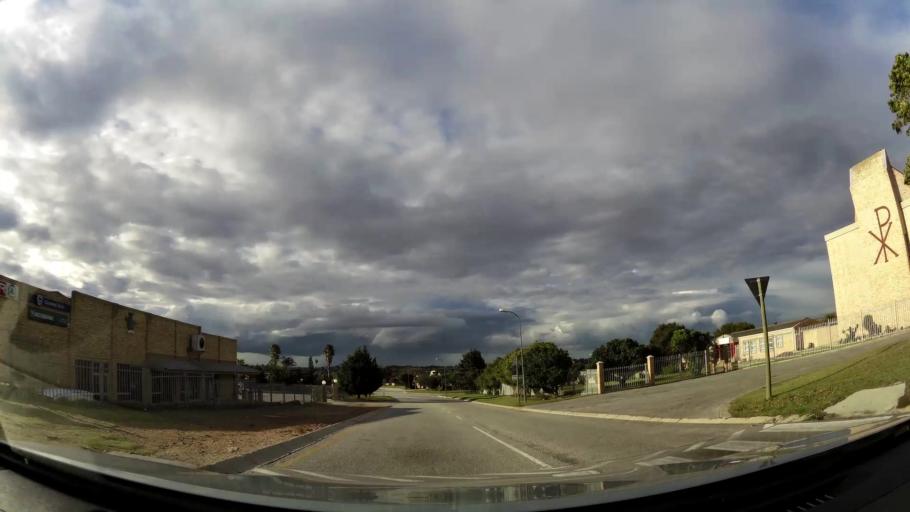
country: ZA
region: Eastern Cape
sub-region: Nelson Mandela Bay Metropolitan Municipality
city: Port Elizabeth
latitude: -33.9590
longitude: 25.4792
